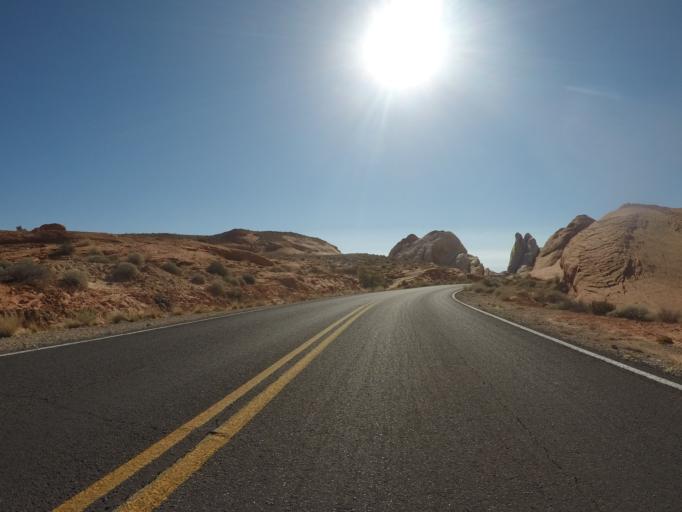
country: US
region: Nevada
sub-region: Clark County
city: Moapa Valley
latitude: 36.4895
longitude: -114.5334
